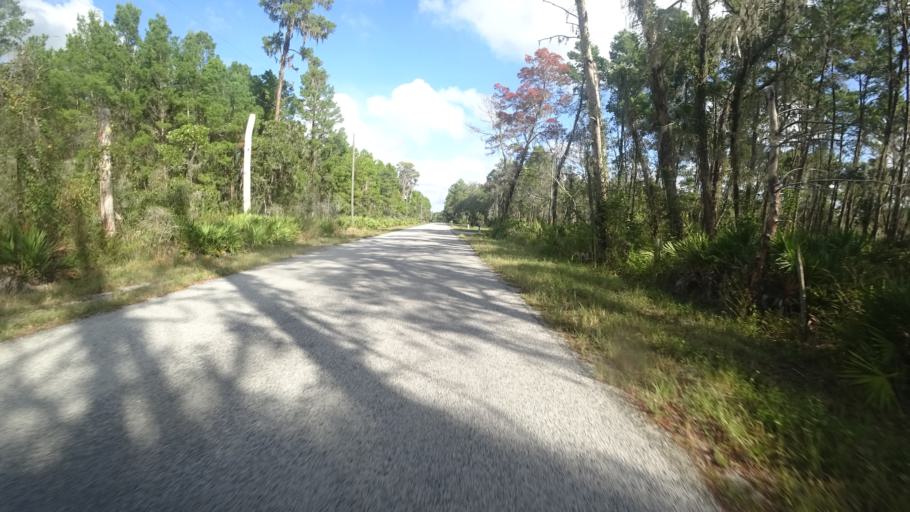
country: US
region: Florida
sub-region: Hillsborough County
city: Wimauma
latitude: 27.4554
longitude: -82.1370
